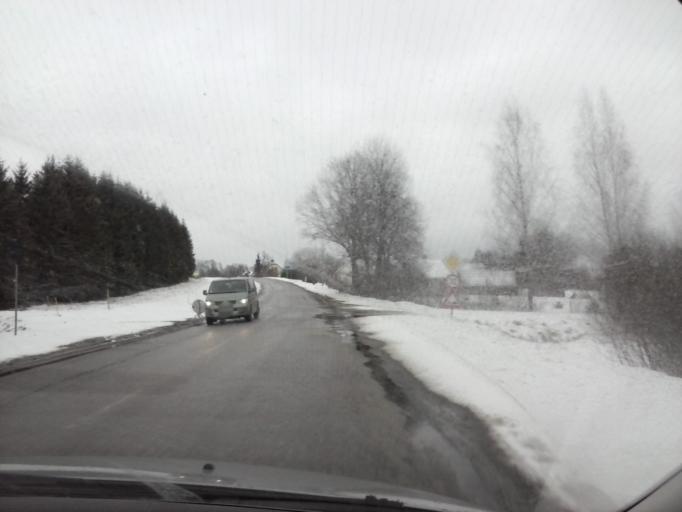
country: LV
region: Valkas Rajons
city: Valka
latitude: 57.7630
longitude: 26.0008
